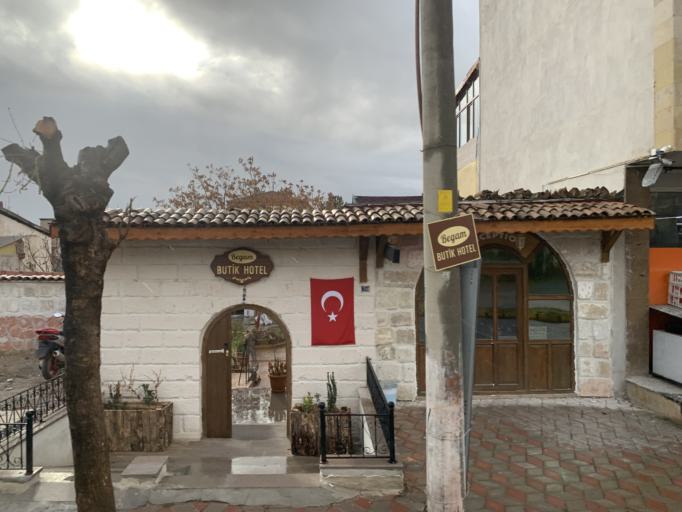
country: TR
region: Nevsehir
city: Avanos
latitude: 38.7199
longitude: 34.8504
